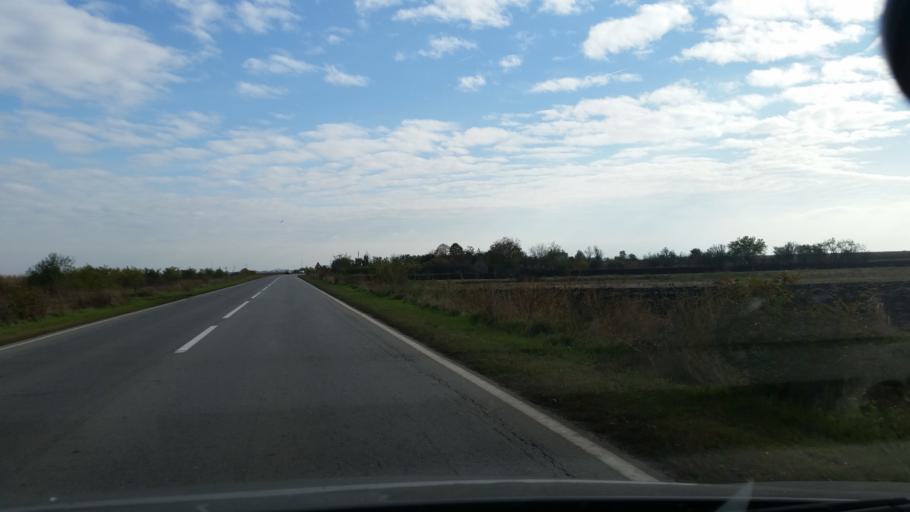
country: RS
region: Autonomna Pokrajina Vojvodina
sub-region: Srednjebanatski Okrug
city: Zrenjanin
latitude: 45.4294
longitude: 20.3690
